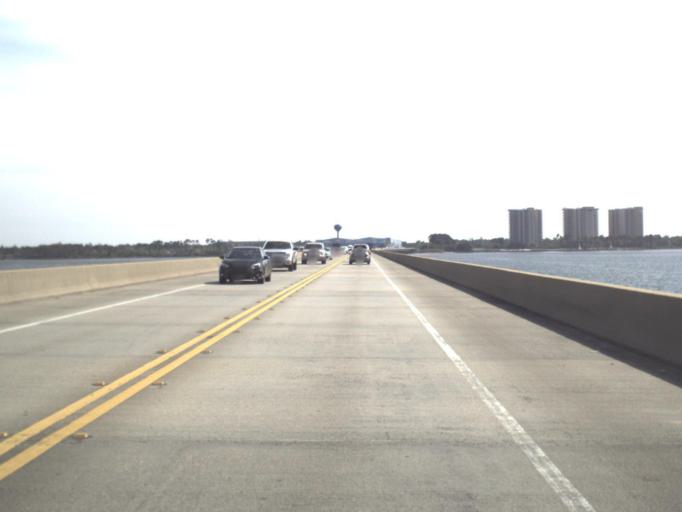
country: US
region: Florida
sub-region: Walton County
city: Miramar Beach
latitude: 30.4136
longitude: -86.4226
